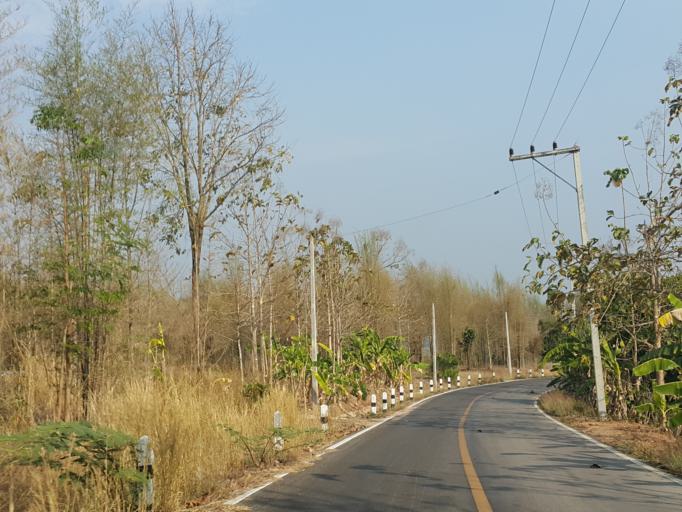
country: TH
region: Lampang
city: Chae Hom
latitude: 18.7252
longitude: 99.5596
